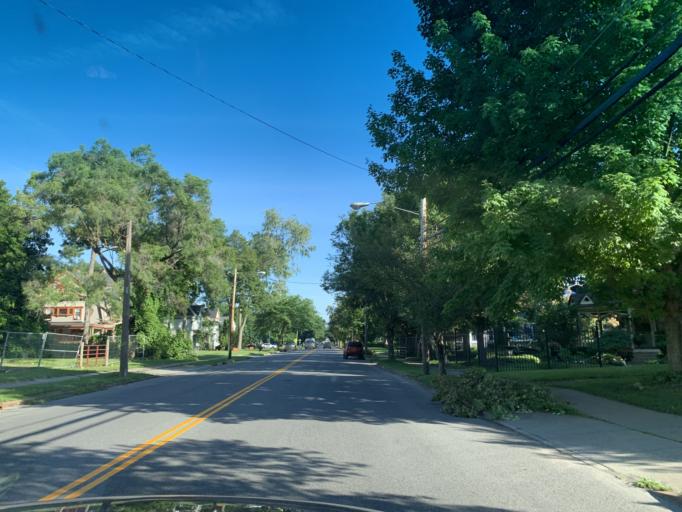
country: US
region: New York
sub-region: Madison County
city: Oneida
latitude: 43.0864
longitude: -75.6467
